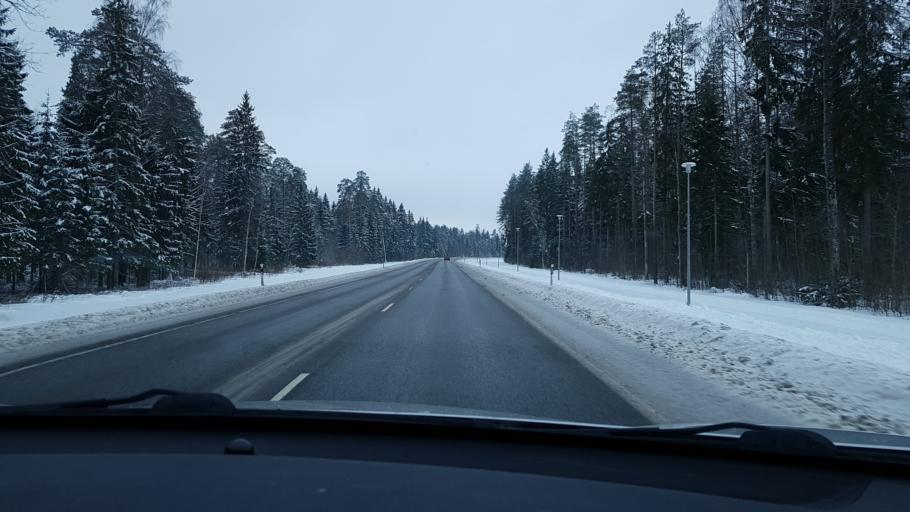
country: EE
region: Jaervamaa
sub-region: Paide linn
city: Paide
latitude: 58.8654
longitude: 25.4927
